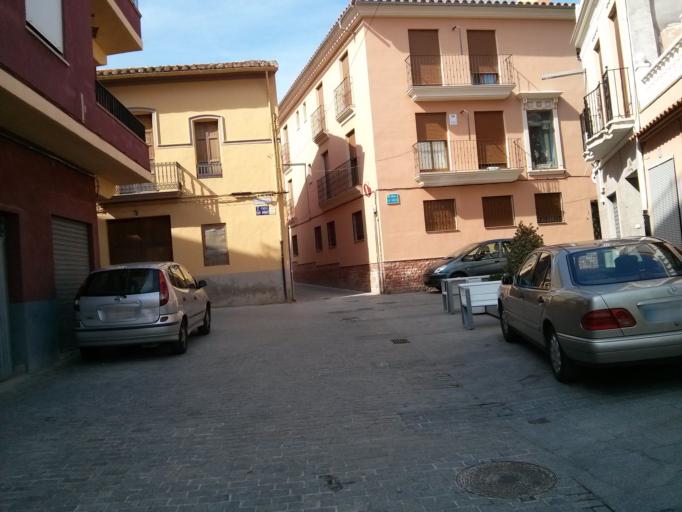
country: ES
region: Valencia
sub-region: Provincia de Castello
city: Alfondeguilla
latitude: 39.8239
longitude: -0.2248
